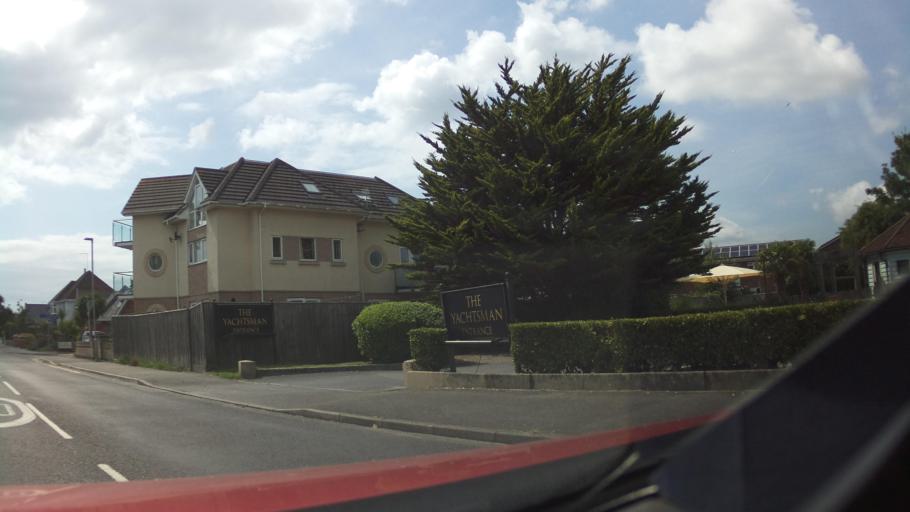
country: GB
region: England
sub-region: Poole
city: Poole
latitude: 50.7141
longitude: -2.0153
